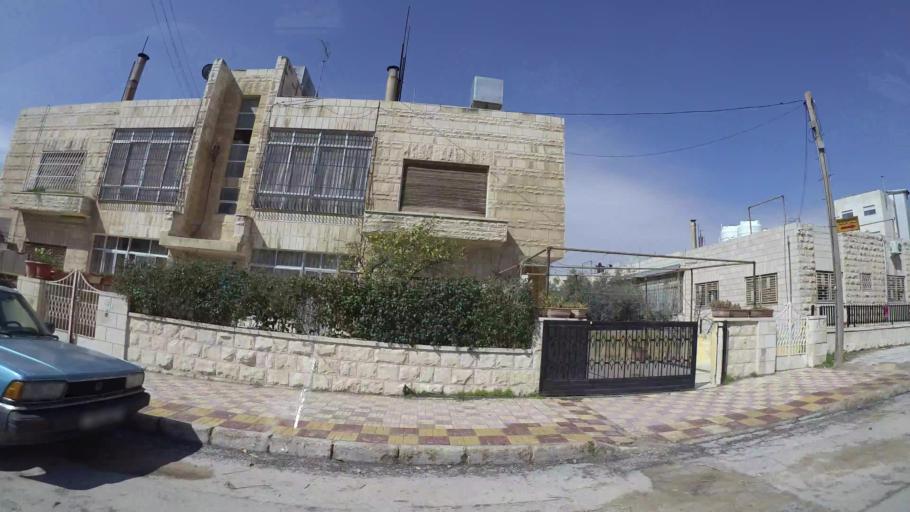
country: JO
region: Amman
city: Al Jubayhah
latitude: 31.9926
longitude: 35.9041
